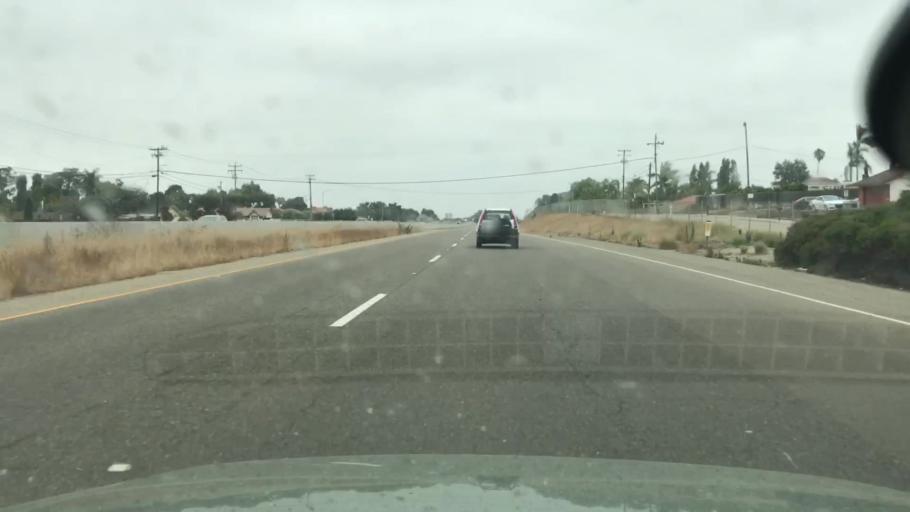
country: US
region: California
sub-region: Santa Barbara County
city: Orcutt
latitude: 34.8679
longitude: -120.4364
